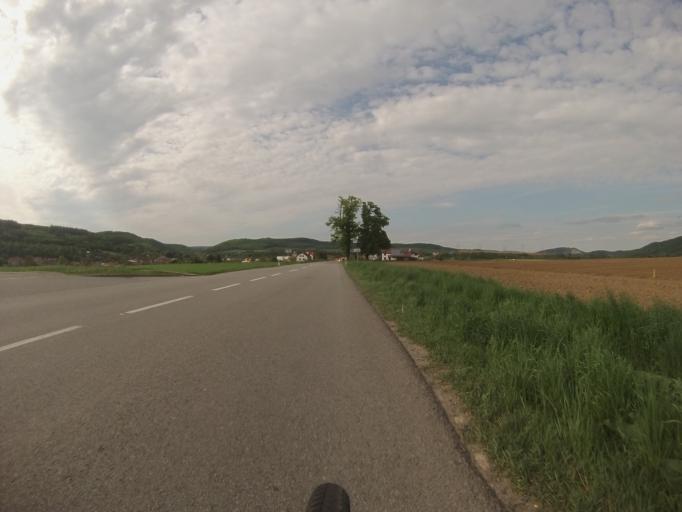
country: CZ
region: South Moravian
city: Veverska Bityska
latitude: 49.2707
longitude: 16.4396
